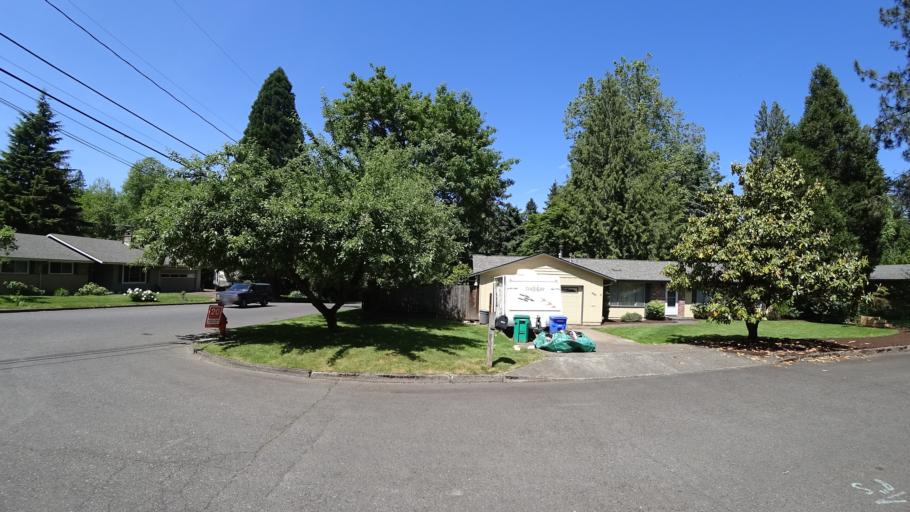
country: US
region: Oregon
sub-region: Clackamas County
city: Lake Oswego
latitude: 45.4572
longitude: -122.7035
